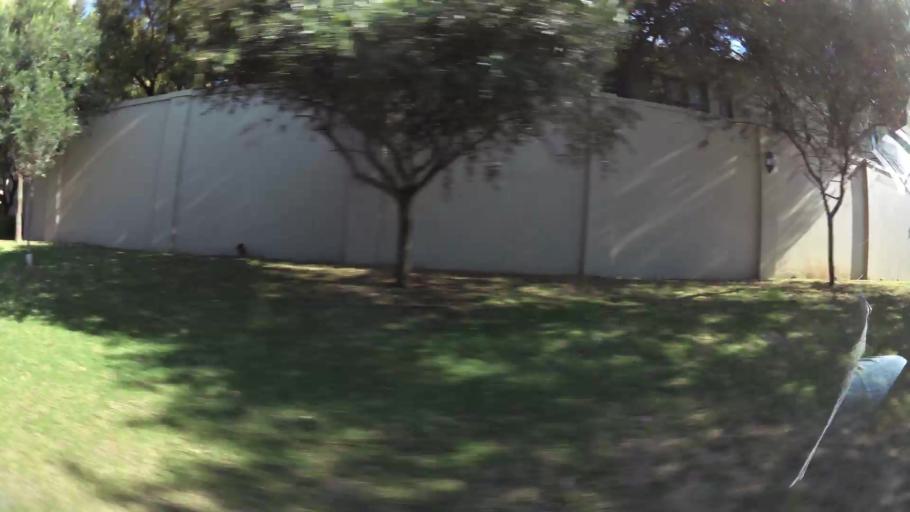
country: ZA
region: Gauteng
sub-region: City of Johannesburg Metropolitan Municipality
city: Midrand
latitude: -26.0549
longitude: 28.0465
